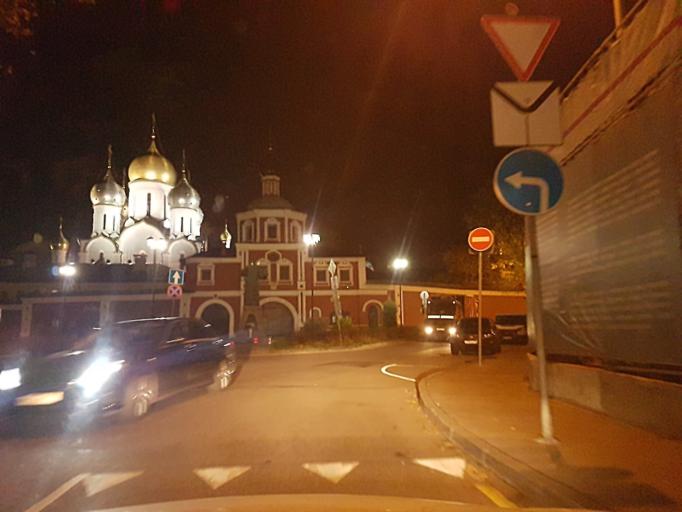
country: RU
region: Moscow
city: Moscow
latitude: 55.7409
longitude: 37.5994
